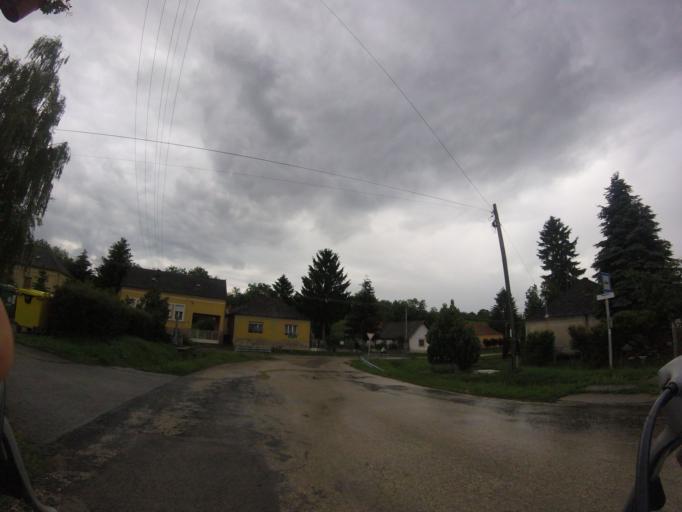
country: HU
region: Baranya
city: Pellerd
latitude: 45.9691
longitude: 18.1682
